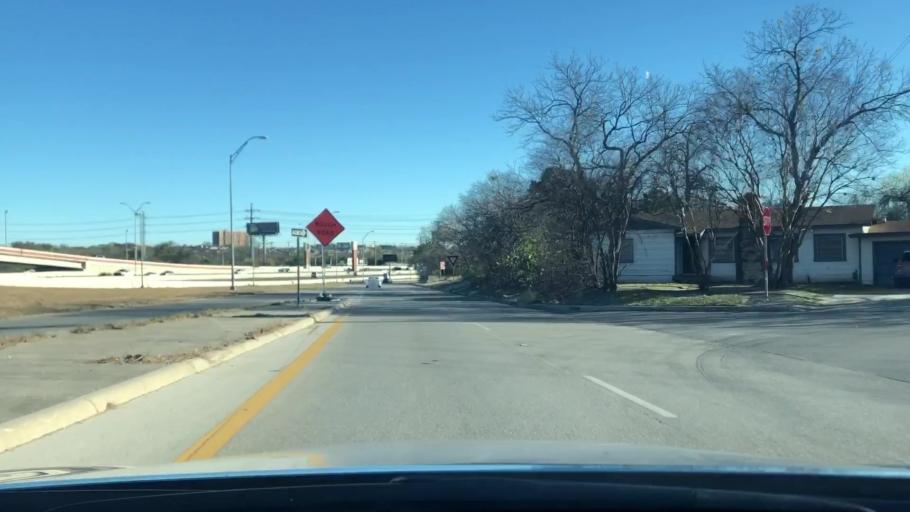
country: US
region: Texas
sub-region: Bexar County
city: Alamo Heights
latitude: 29.5142
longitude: -98.4778
